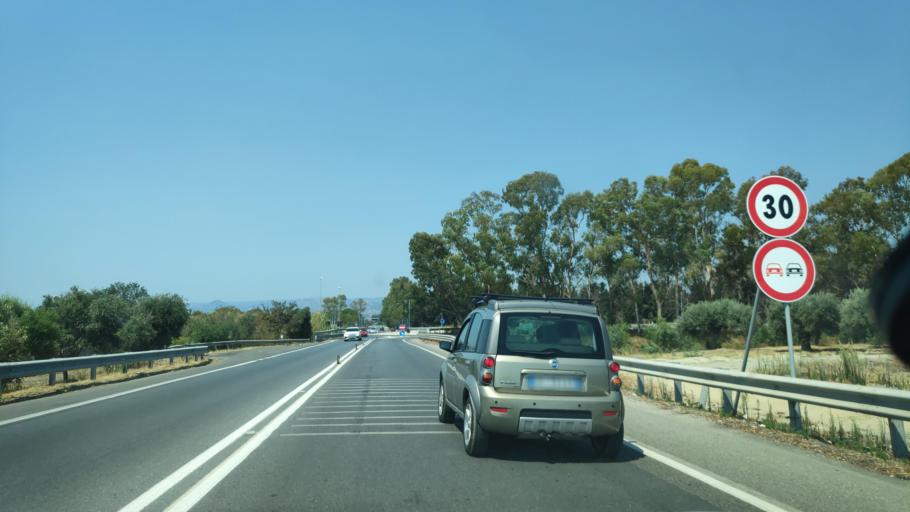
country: IT
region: Calabria
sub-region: Provincia di Reggio Calabria
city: Marina di Gioiosa Ionica
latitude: 38.3061
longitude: 16.3543
